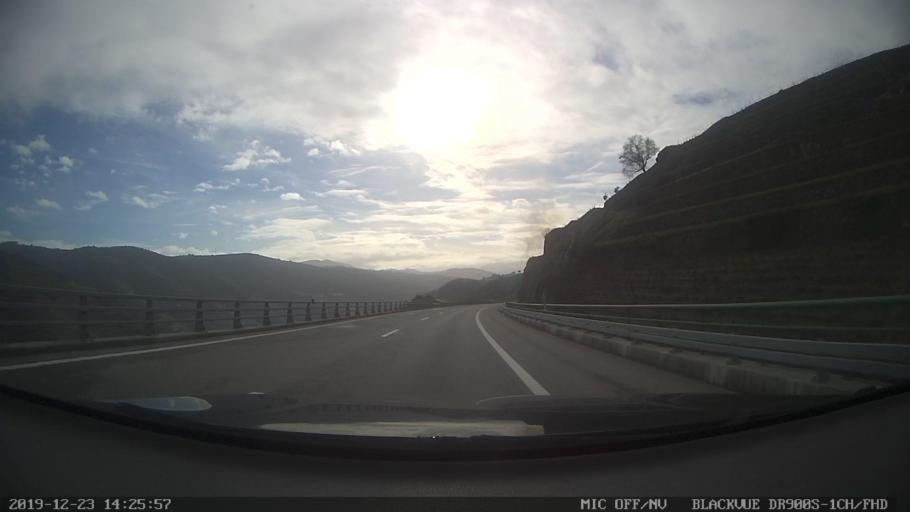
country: PT
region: Vila Real
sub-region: Peso da Regua
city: Peso da Regua
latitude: 41.1867
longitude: -7.7491
